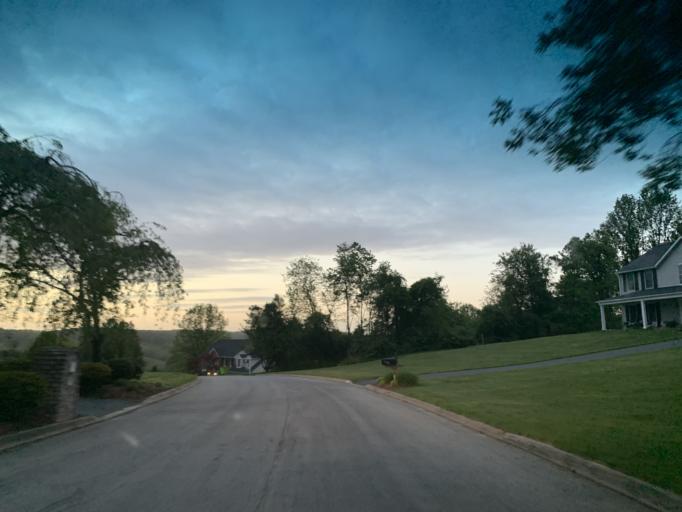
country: US
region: Maryland
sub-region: Harford County
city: South Bel Air
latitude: 39.5930
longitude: -76.2660
